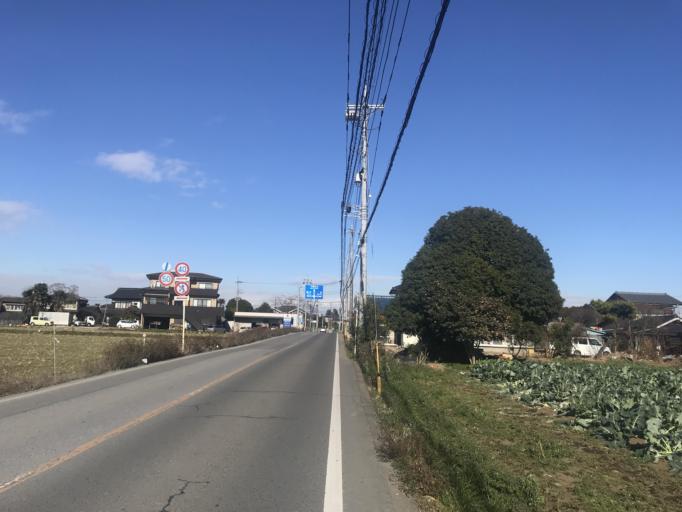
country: JP
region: Ibaraki
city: Yuki
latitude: 36.3671
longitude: 139.8772
